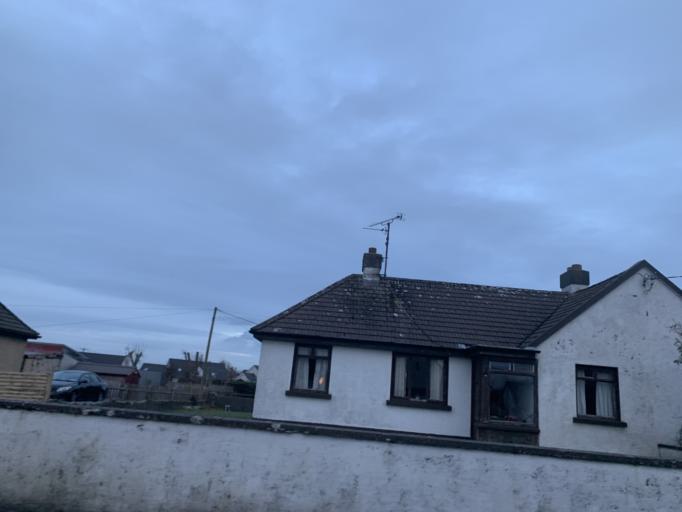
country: IE
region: Connaught
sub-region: Sligo
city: Collooney
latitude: 54.1819
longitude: -8.4919
